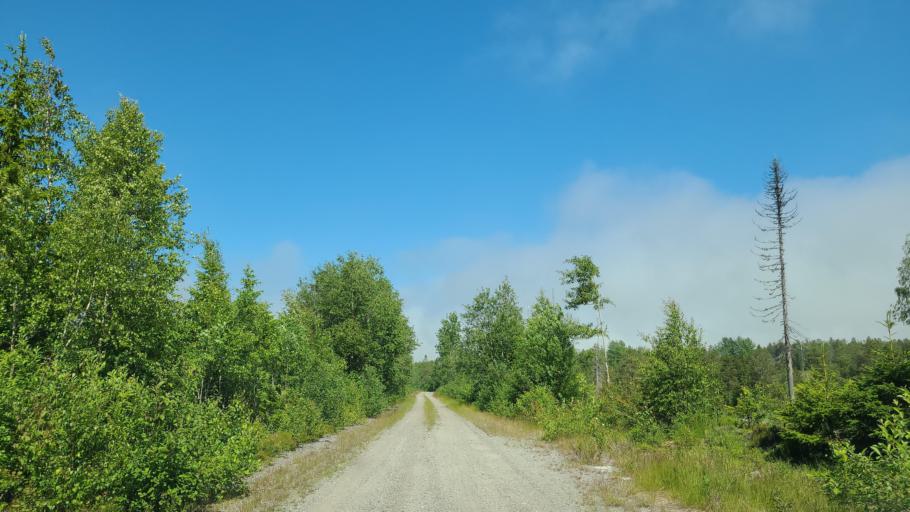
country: SE
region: Vaesternorrland
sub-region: OErnskoeldsviks Kommun
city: Husum
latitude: 63.4432
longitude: 19.2351
